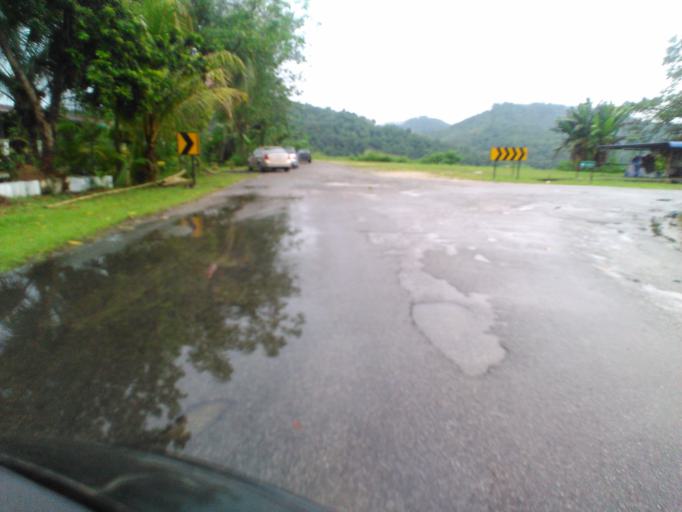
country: MY
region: Kedah
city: Kulim
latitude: 5.3643
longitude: 100.5720
